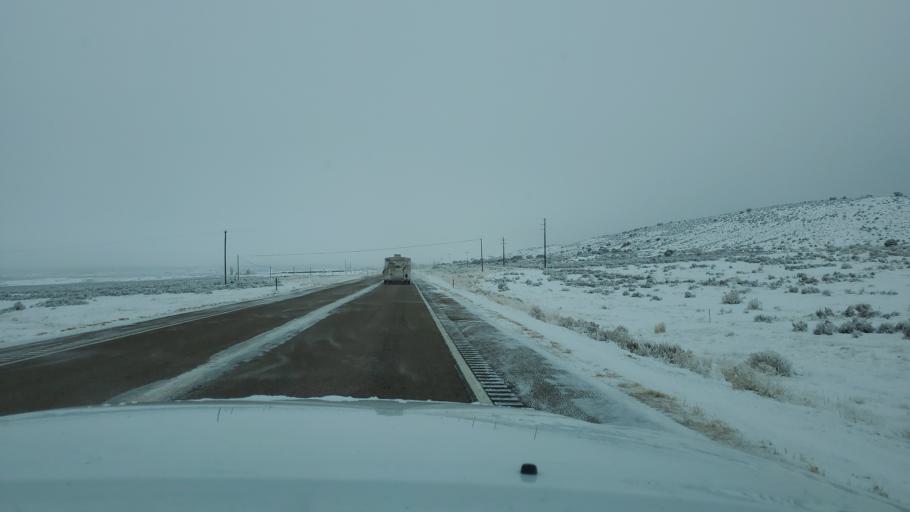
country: US
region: Colorado
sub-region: Rio Blanco County
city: Rangely
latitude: 40.2430
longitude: -108.9783
